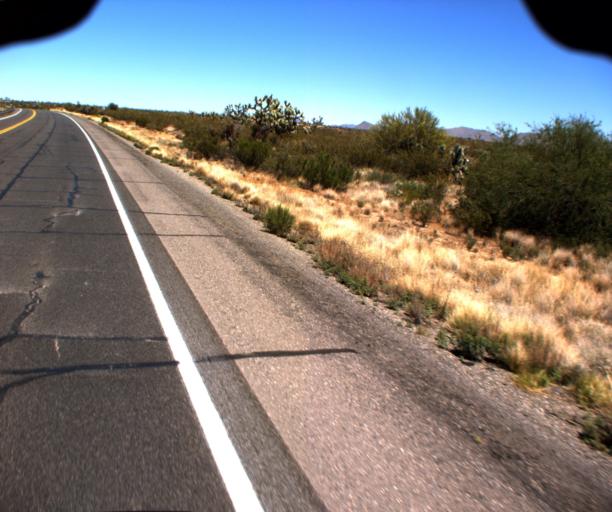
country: US
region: Arizona
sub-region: Yavapai County
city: Congress
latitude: 34.2262
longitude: -113.0695
